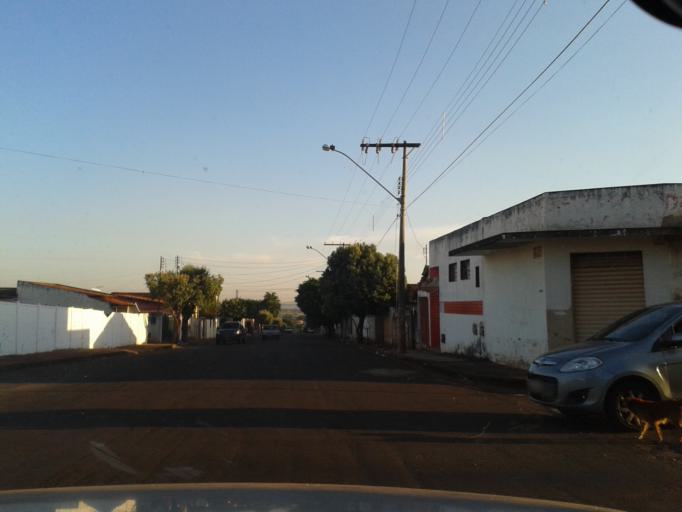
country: BR
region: Minas Gerais
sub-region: Ituiutaba
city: Ituiutaba
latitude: -18.9830
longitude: -49.4678
